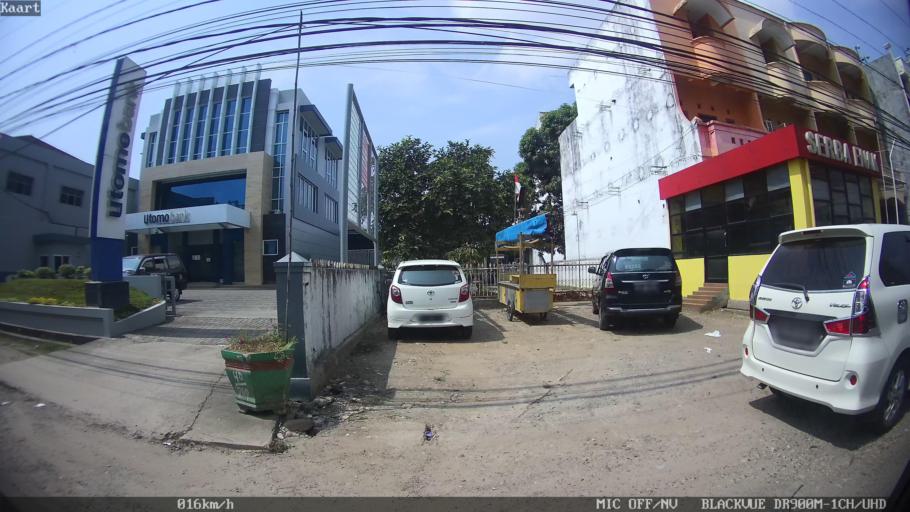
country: ID
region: Lampung
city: Pringsewu
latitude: -5.3564
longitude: 104.9798
